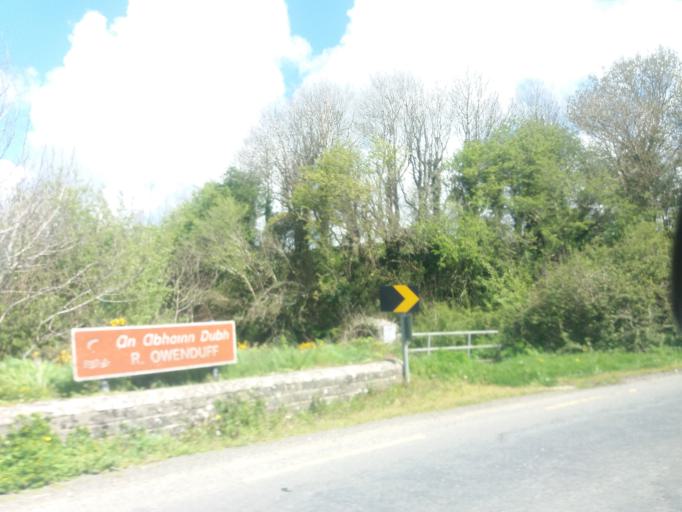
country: IE
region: Leinster
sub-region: Loch Garman
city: New Ross
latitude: 52.2675
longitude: -6.7729
